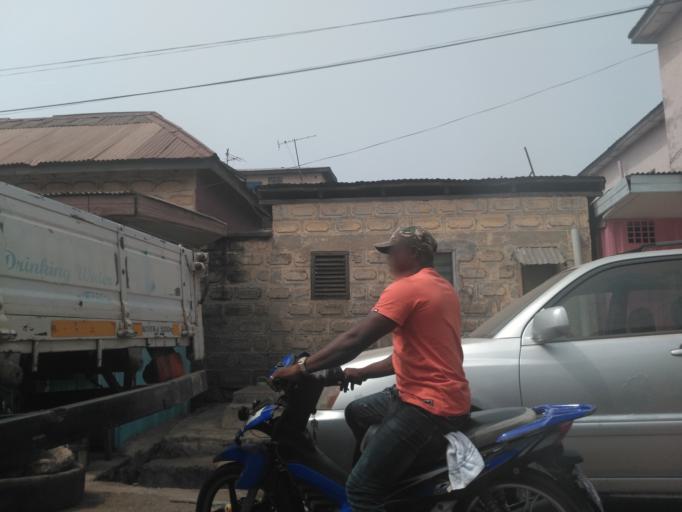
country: GH
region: Ashanti
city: Kumasi
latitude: 6.7018
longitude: -1.6143
